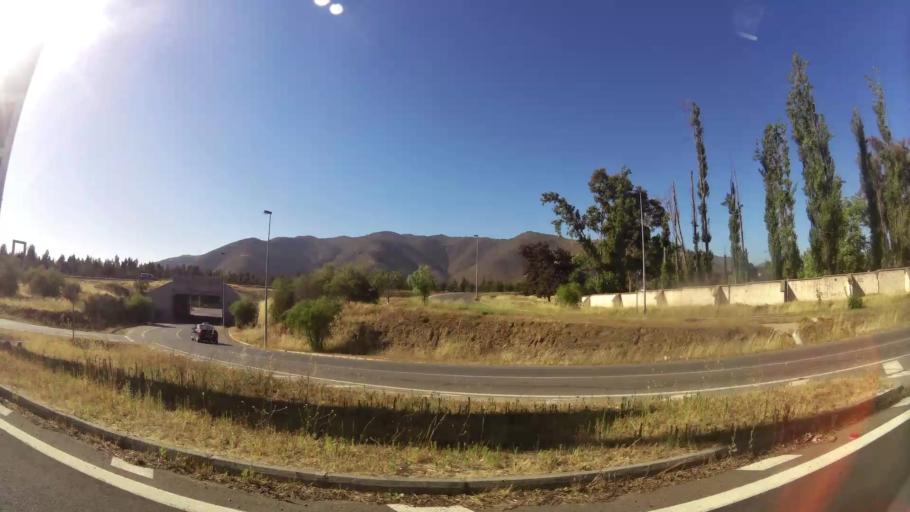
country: CL
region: Santiago Metropolitan
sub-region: Provincia de Chacabuco
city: Lampa
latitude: -33.4015
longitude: -71.1190
